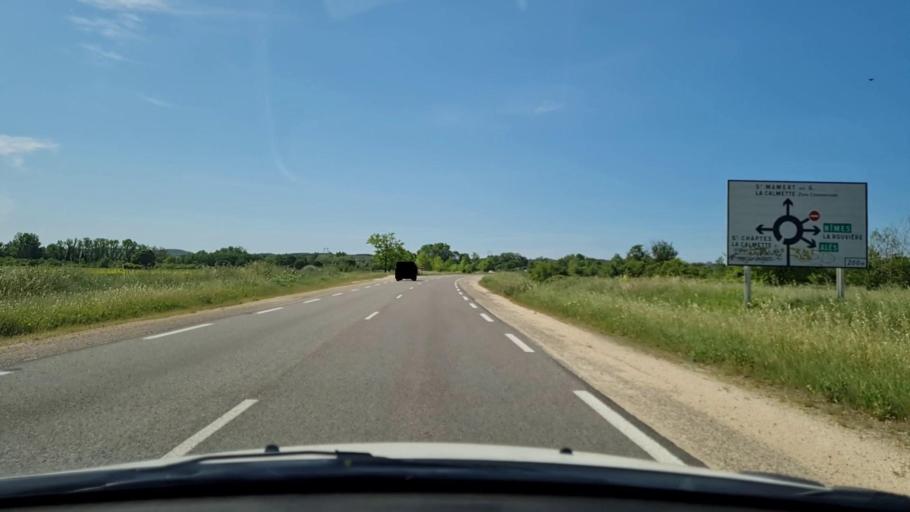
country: FR
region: Languedoc-Roussillon
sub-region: Departement du Gard
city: La Calmette
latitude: 43.9362
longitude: 4.2555
